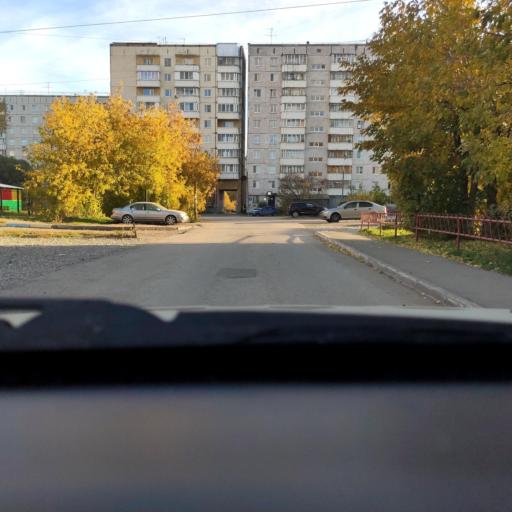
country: RU
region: Perm
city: Kondratovo
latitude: 57.9990
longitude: 56.1415
